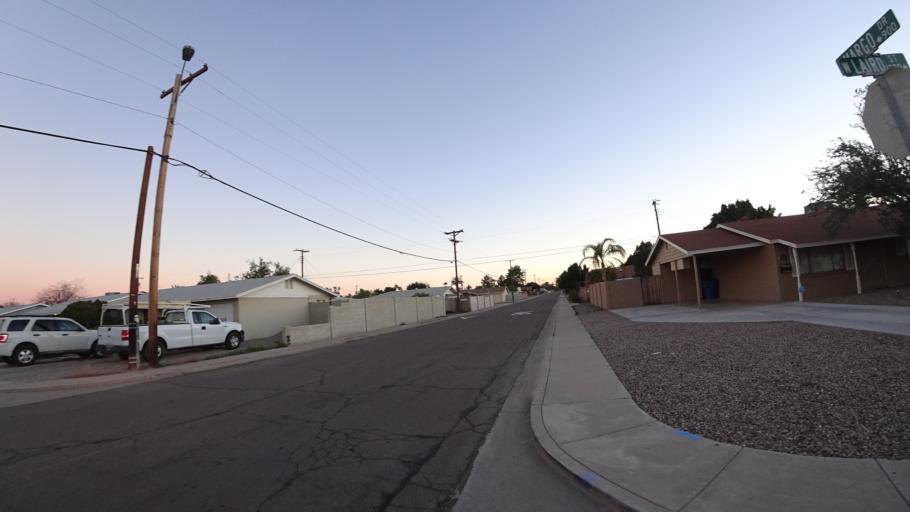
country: US
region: Arizona
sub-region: Maricopa County
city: Tempe Junction
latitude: 33.4203
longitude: -111.9587
